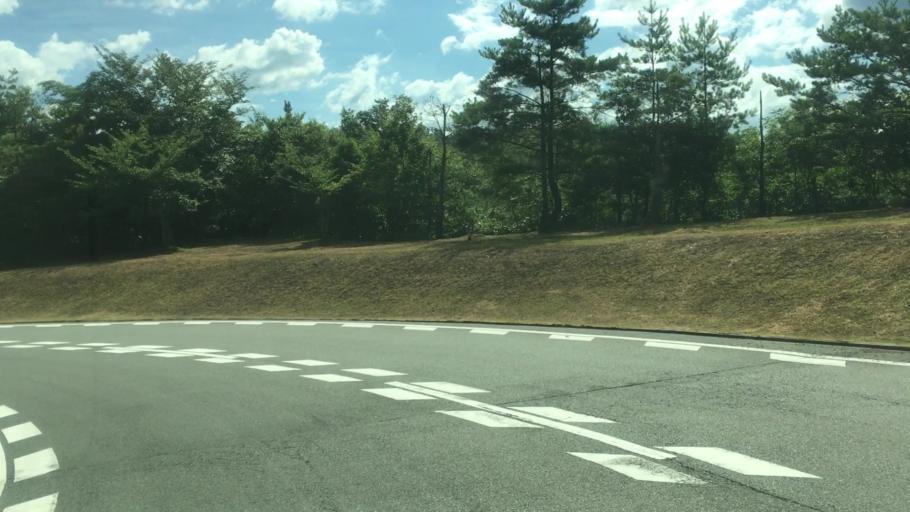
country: JP
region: Hyogo
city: Toyooka
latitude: 35.5237
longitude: 134.7912
